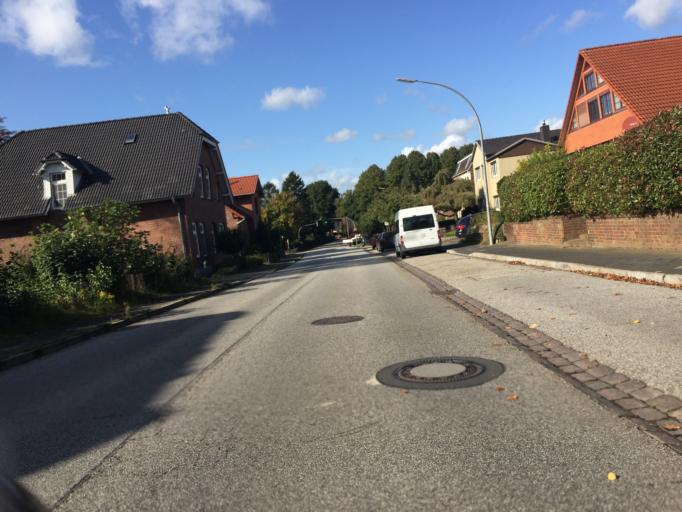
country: DE
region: Schleswig-Holstein
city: Itzehoe
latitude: 53.9277
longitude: 9.5045
